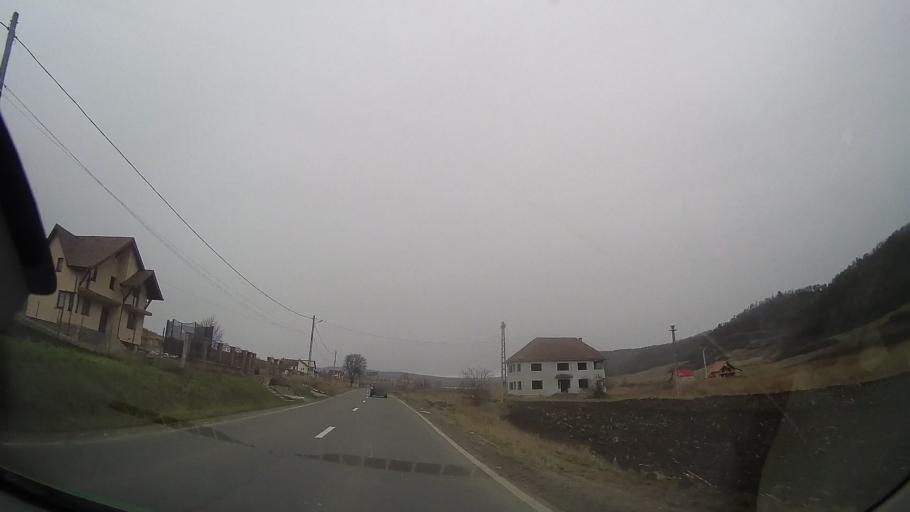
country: RO
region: Mures
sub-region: Comuna Ceausu de Campie
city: Ceausu de Campie
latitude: 46.6210
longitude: 24.5240
